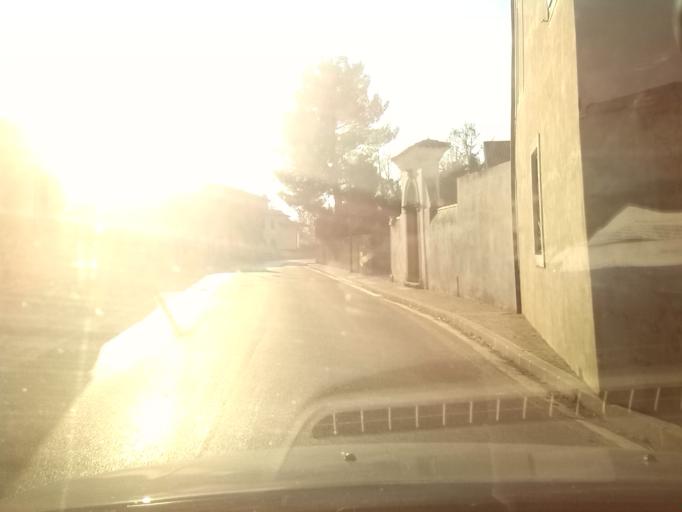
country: IT
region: Friuli Venezia Giulia
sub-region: Provincia di Udine
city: Santa Maria la Longa
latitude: 45.9326
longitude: 13.2819
